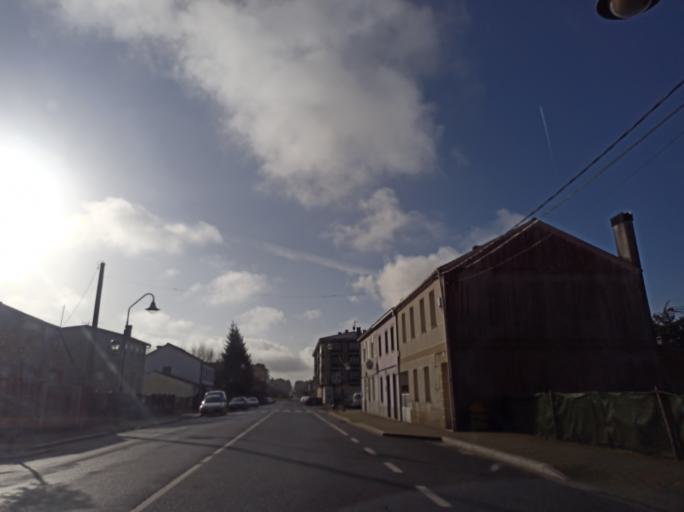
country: ES
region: Galicia
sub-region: Provincia da Coruna
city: Curtis
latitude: 43.1363
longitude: -8.0353
